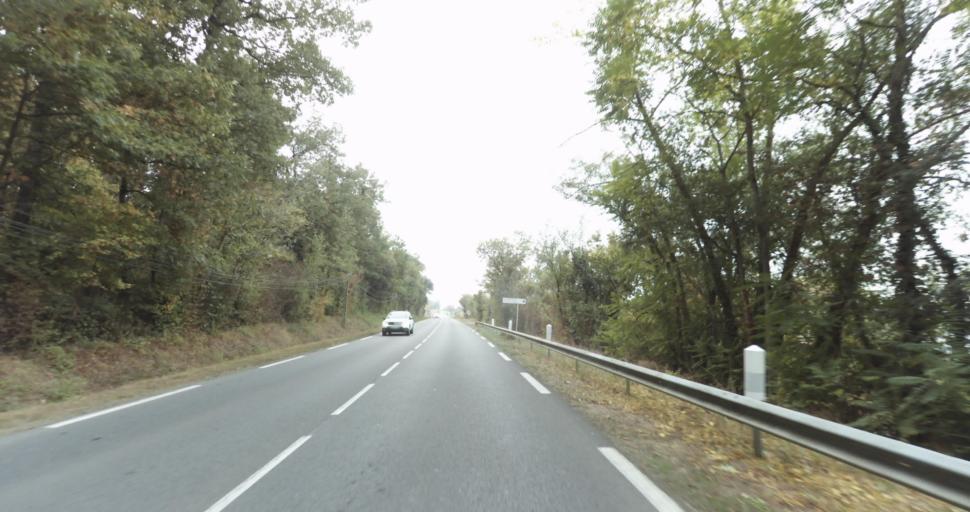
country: FR
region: Midi-Pyrenees
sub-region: Departement du Gers
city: Preignan
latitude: 43.6905
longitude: 0.6049
